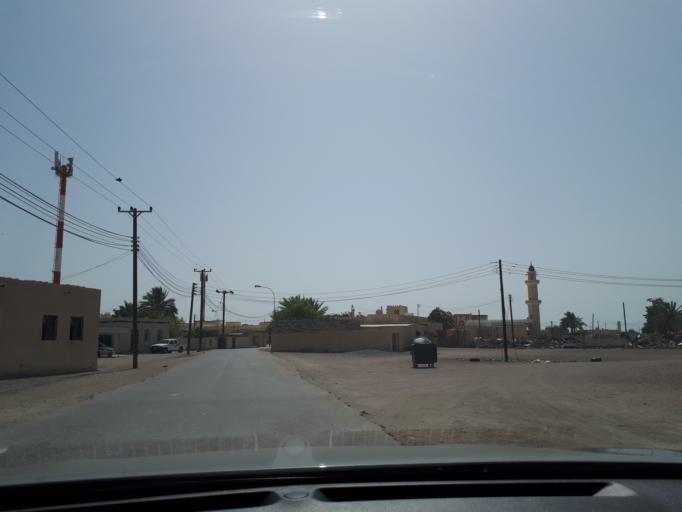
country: OM
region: Al Batinah
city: Barka'
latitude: 23.7067
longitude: 57.9321
